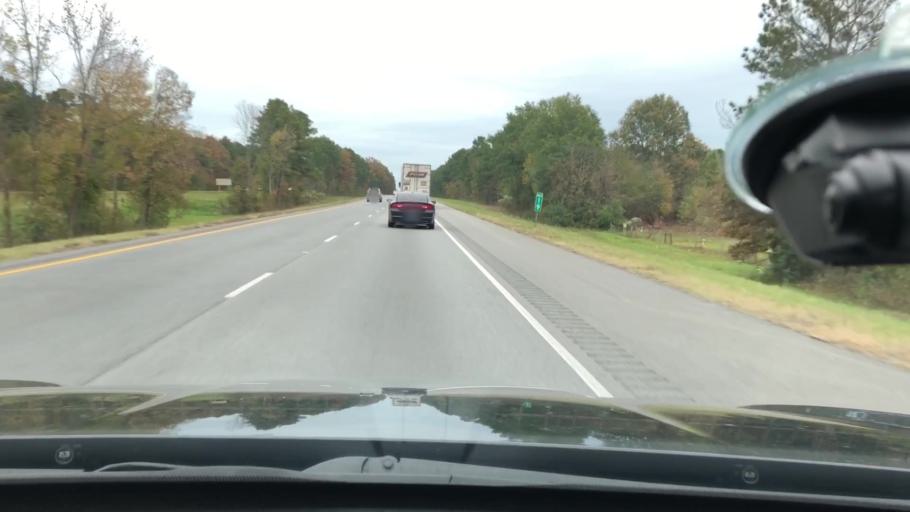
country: US
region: Arkansas
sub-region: Hempstead County
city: Hope
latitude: 33.6211
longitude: -93.7835
